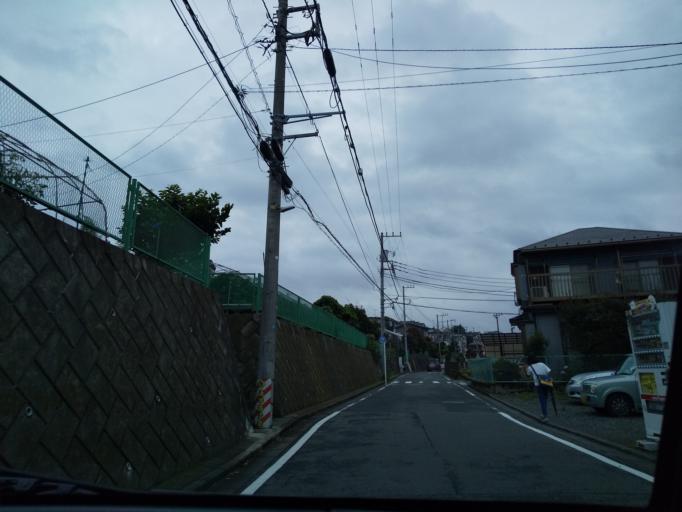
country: JP
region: Kanagawa
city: Fujisawa
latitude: 35.3936
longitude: 139.5150
